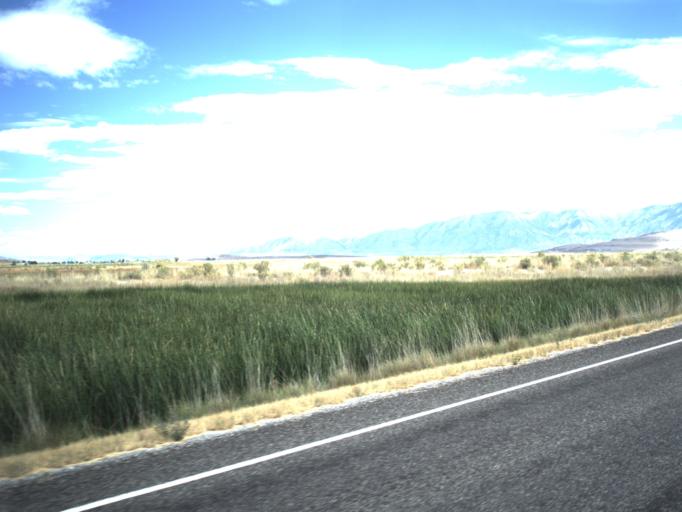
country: US
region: Utah
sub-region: Box Elder County
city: Tremonton
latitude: 41.6112
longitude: -112.3529
